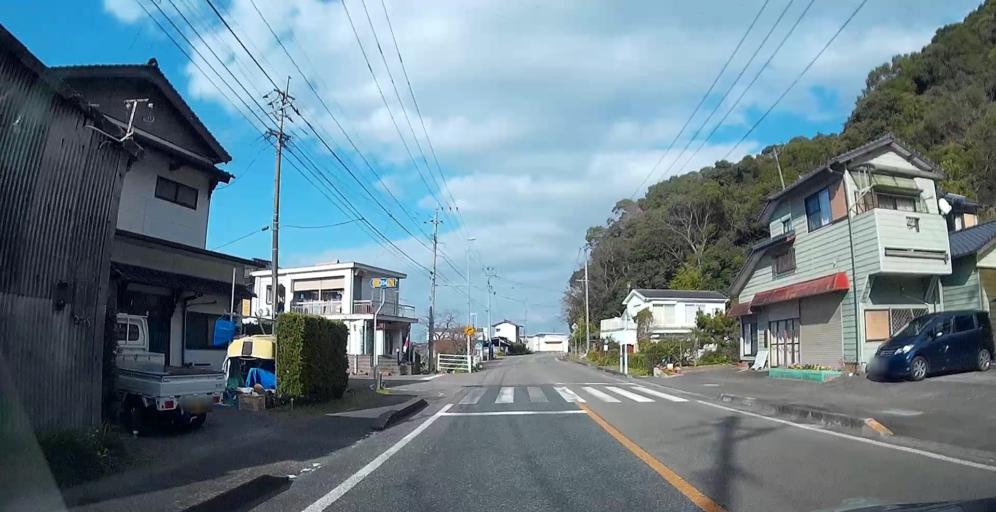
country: JP
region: Kumamoto
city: Yatsushiro
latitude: 32.4196
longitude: 130.5509
